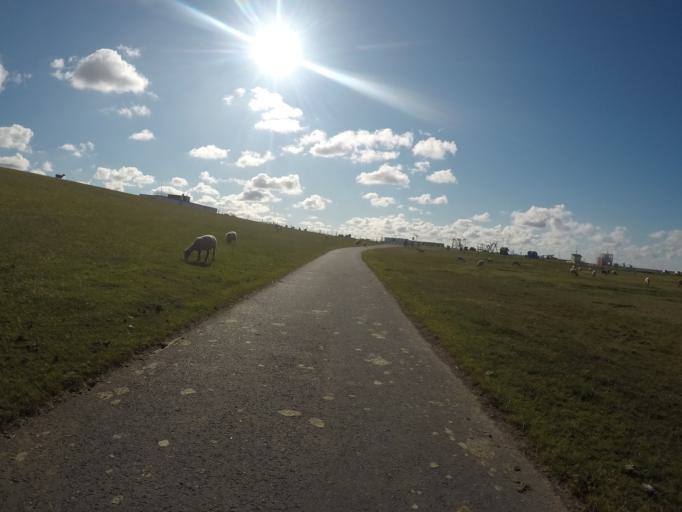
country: DE
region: Lower Saxony
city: Nordleda
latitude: 53.8339
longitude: 8.7837
